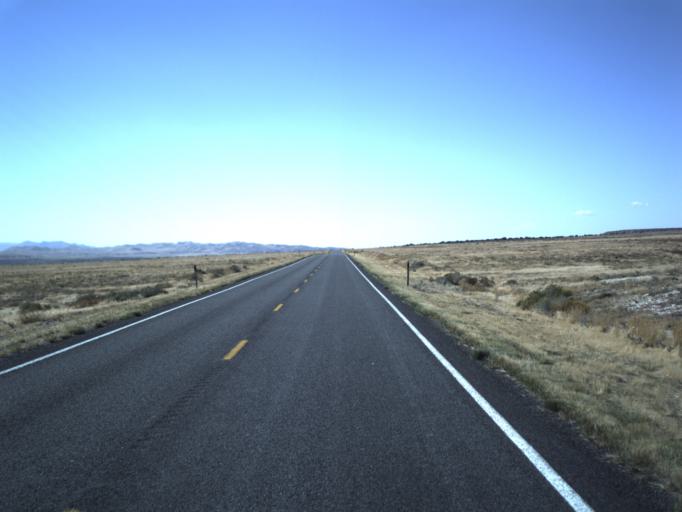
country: US
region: Utah
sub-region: Beaver County
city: Milford
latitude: 38.8592
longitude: -112.8393
